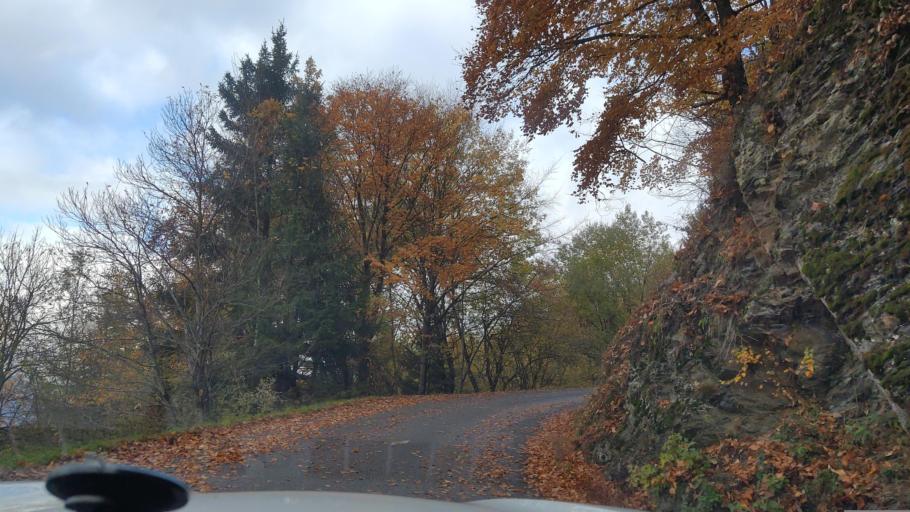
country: FR
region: Rhone-Alpes
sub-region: Departement de la Savoie
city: Albertville
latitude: 45.6791
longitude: 6.4192
